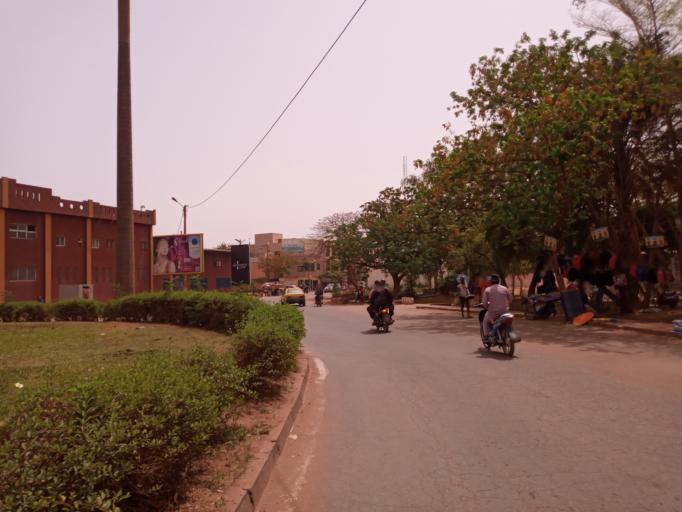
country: ML
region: Bamako
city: Bamako
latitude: 12.6430
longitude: -7.9789
